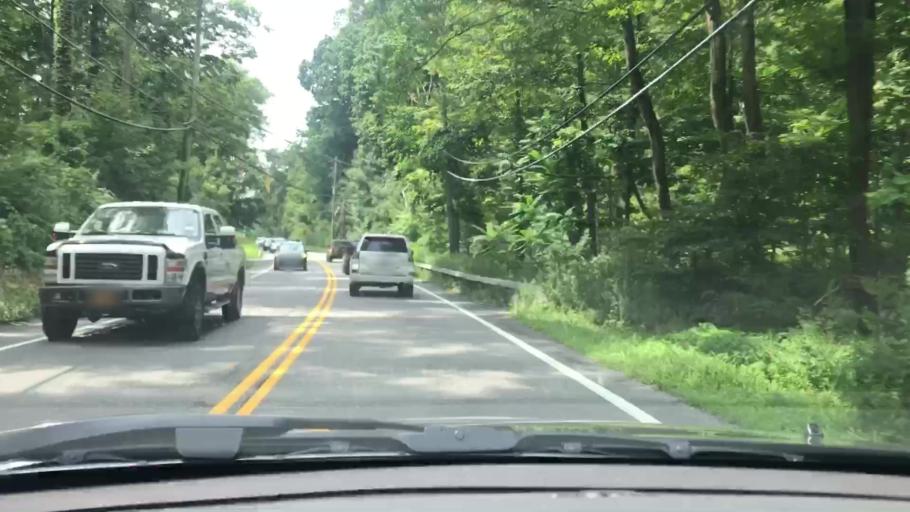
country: US
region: New York
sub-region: Westchester County
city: Mount Kisco
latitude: 41.2002
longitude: -73.7135
